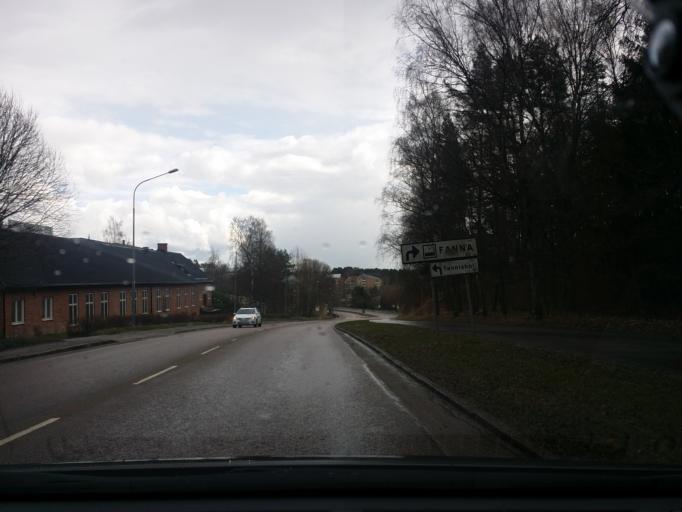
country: SE
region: Uppsala
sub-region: Enkopings Kommun
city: Enkoping
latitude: 59.6430
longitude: 17.0912
